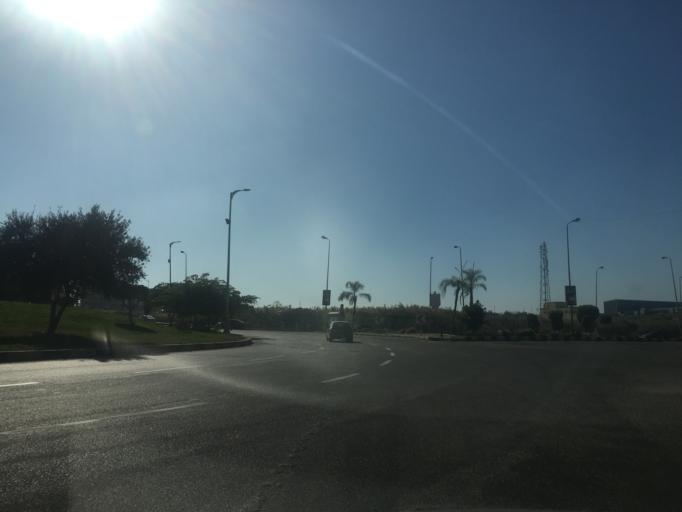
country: EG
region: Al Jizah
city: Awsim
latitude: 30.0217
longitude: 30.9816
